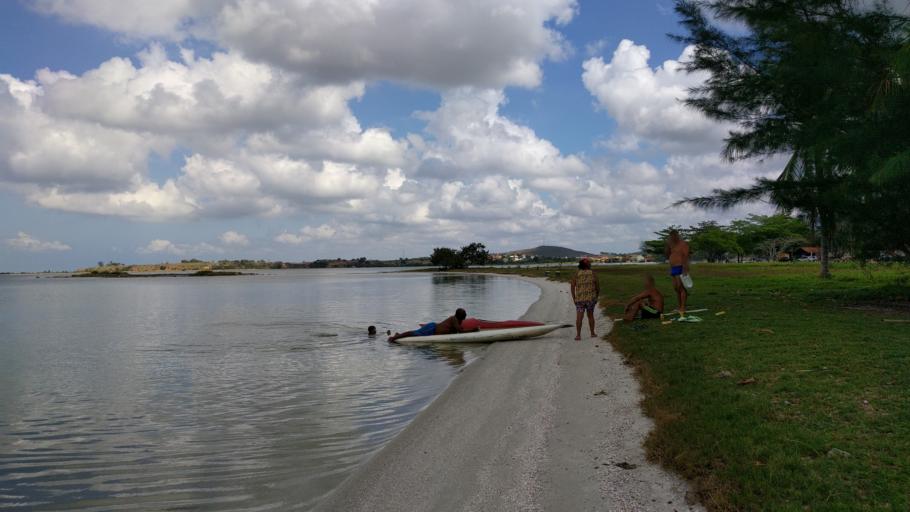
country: BR
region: Rio de Janeiro
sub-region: Sao Pedro Da Aldeia
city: Sao Pedro da Aldeia
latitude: -22.8422
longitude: -42.1286
